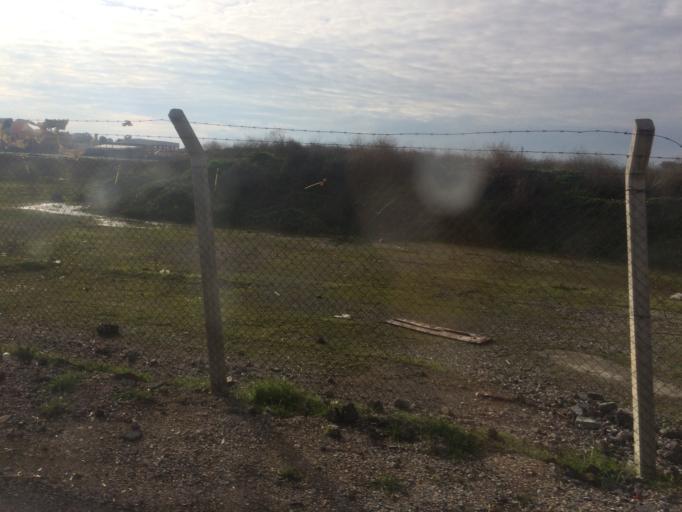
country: TR
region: Izmir
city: Menemen
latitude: 38.4969
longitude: 26.9601
